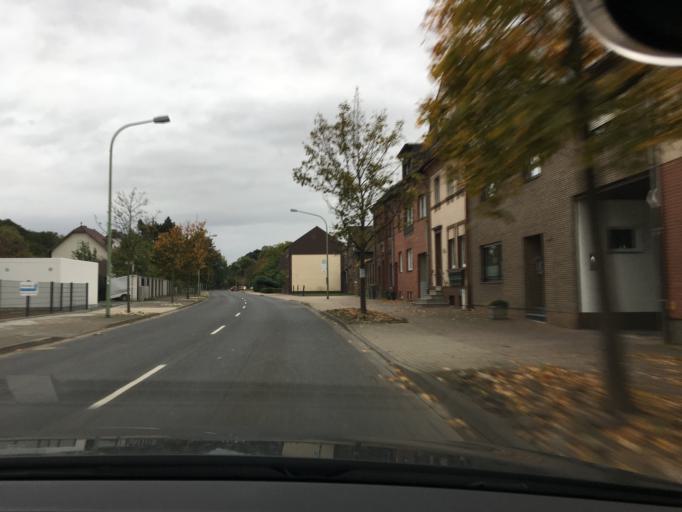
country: DE
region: North Rhine-Westphalia
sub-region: Regierungsbezirk Koln
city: Kreuzau
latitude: 50.7443
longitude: 6.4950
